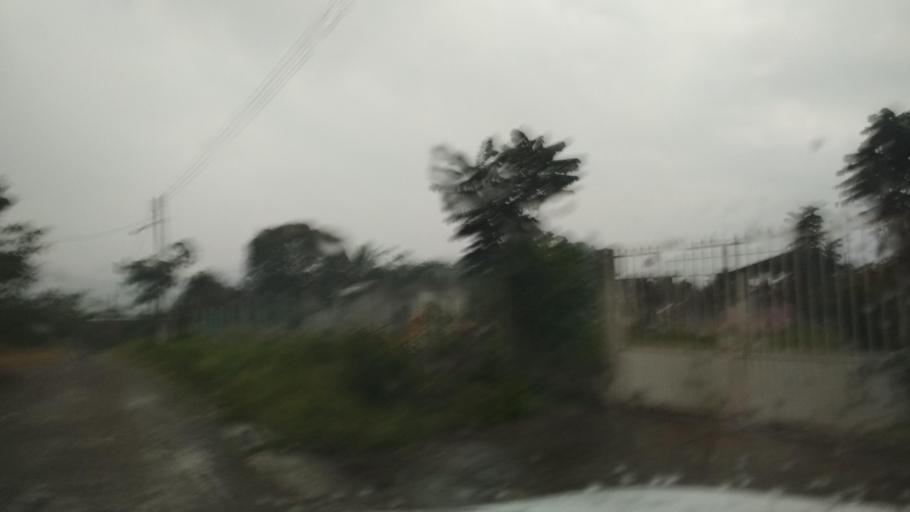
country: MM
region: Shan
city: Taunggyi
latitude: 20.3022
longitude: 97.3043
